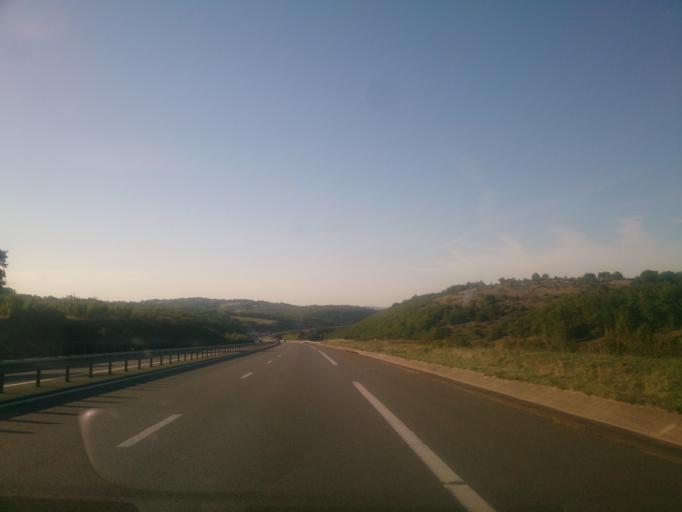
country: FR
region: Midi-Pyrenees
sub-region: Departement du Lot
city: Le Vigan
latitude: 44.7179
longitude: 1.5664
